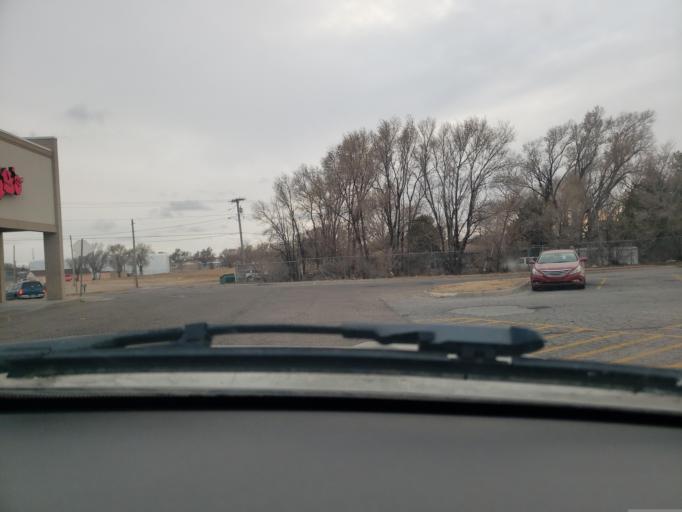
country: US
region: Kansas
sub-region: Finney County
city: Garden City
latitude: 37.9755
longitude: -100.8434
